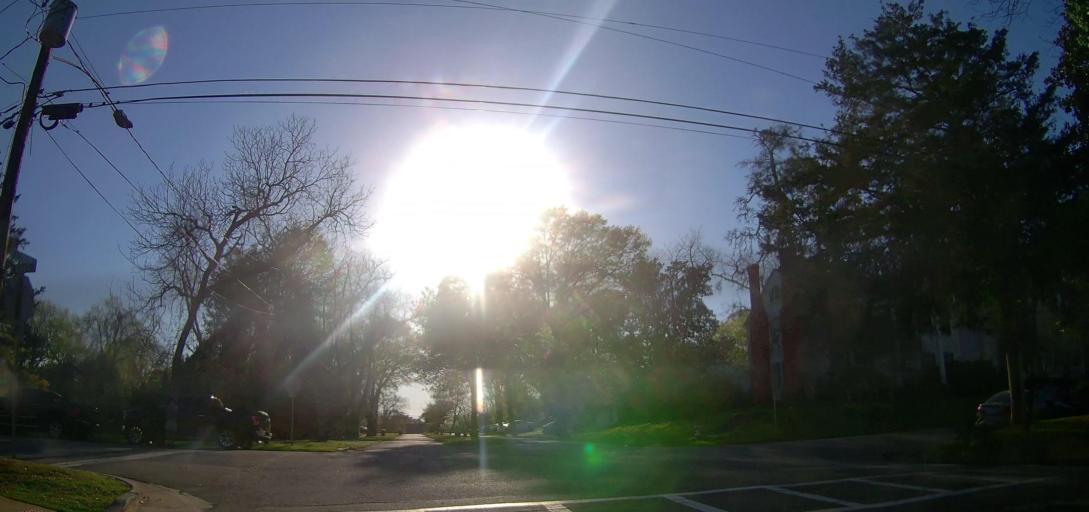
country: US
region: Georgia
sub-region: Baldwin County
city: Milledgeville
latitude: 33.0779
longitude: -83.2296
